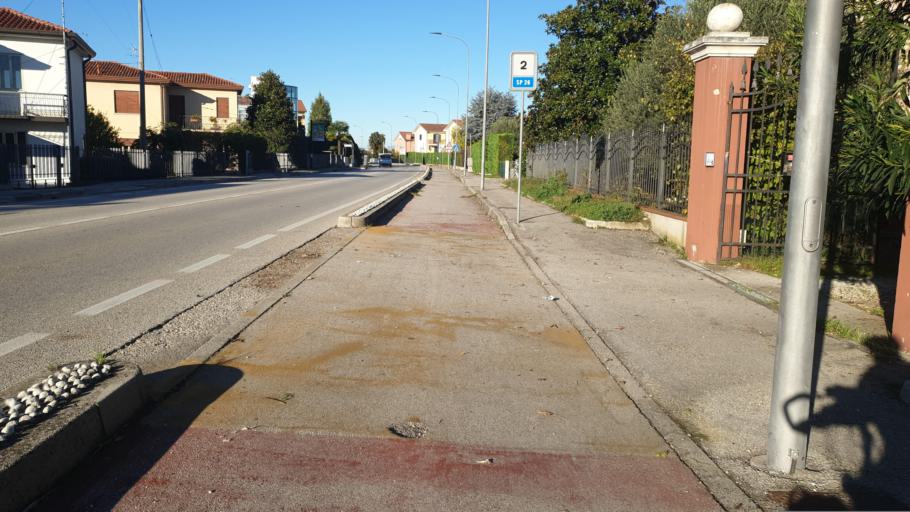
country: IT
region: Veneto
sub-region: Provincia di Venezia
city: Cazzago-Ex Polo
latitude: 45.4420
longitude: 12.0746
